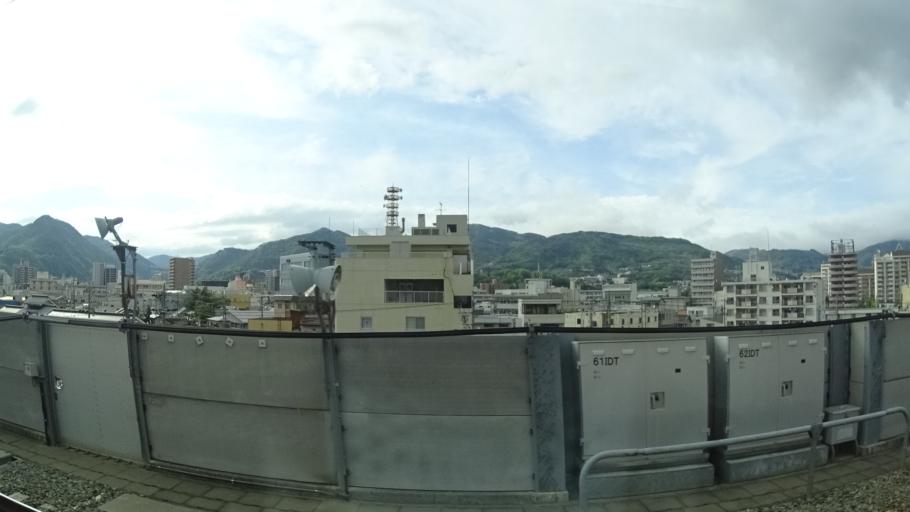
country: JP
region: Nagano
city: Nagano-shi
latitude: 36.6517
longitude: 138.2011
